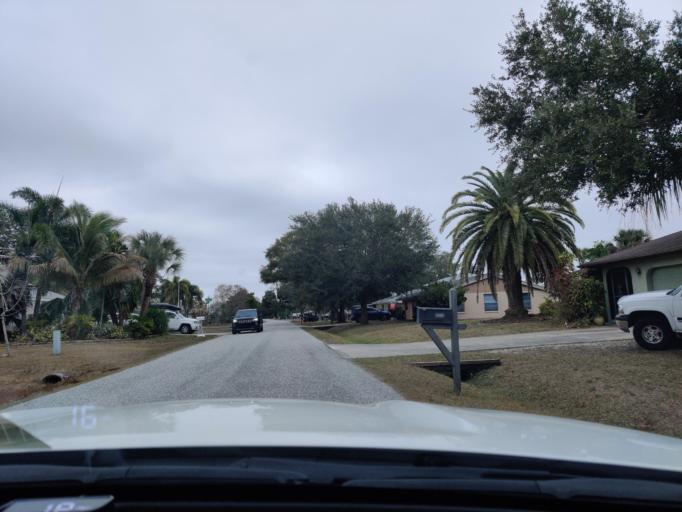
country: US
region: Florida
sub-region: Sarasota County
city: South Venice
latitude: 27.0388
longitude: -82.4023
